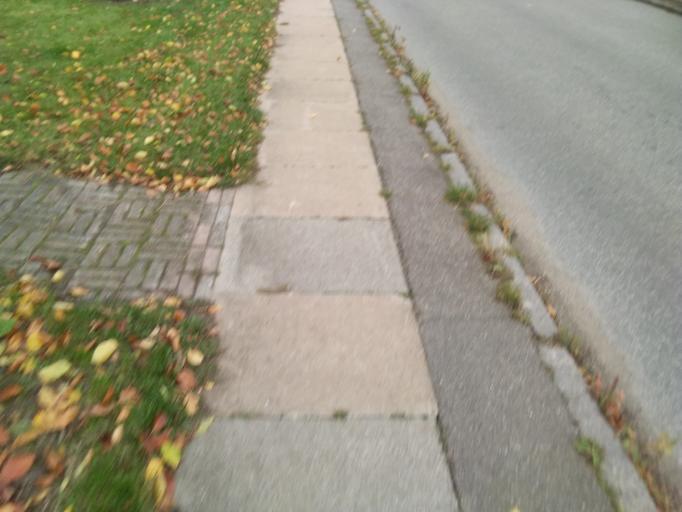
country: DK
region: Capital Region
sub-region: Rodovre Kommune
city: Rodovre
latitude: 55.7049
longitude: 12.4661
